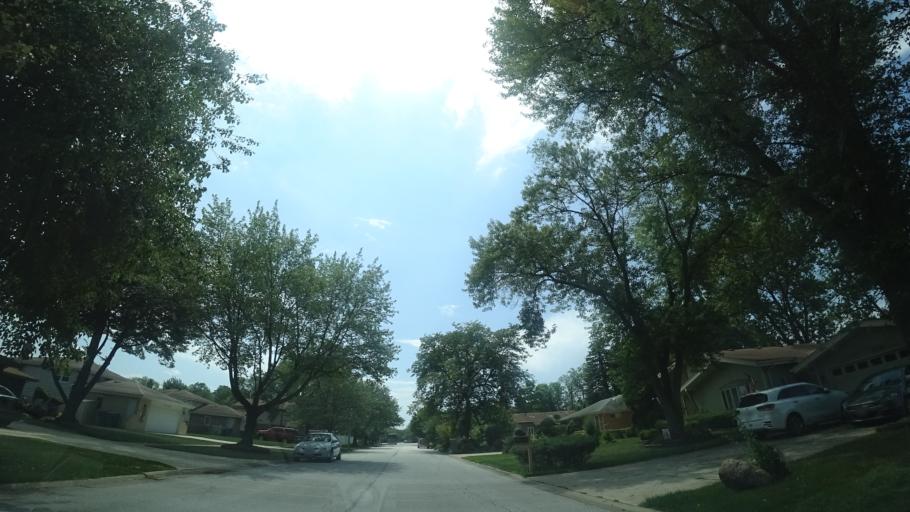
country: US
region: Illinois
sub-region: Cook County
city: Crestwood
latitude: 41.6625
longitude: -87.7680
